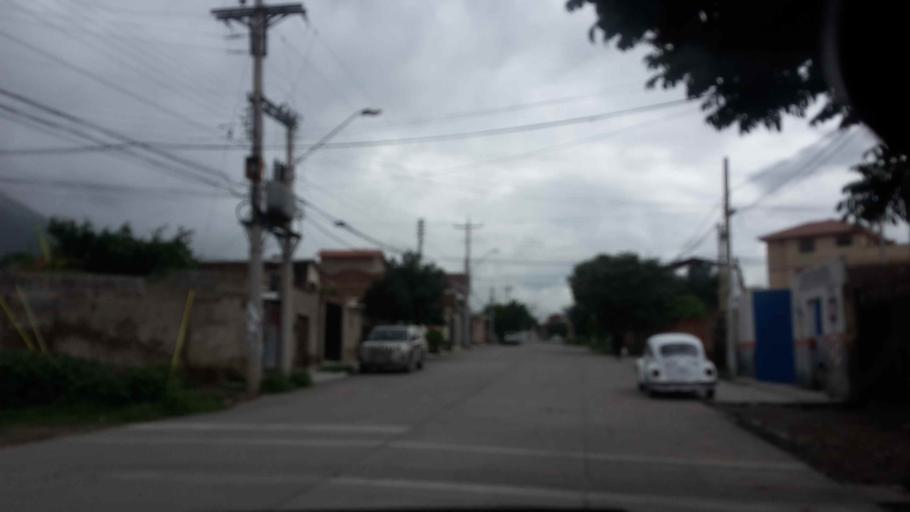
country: BO
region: Cochabamba
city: Cochabamba
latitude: -17.3763
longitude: -66.1236
